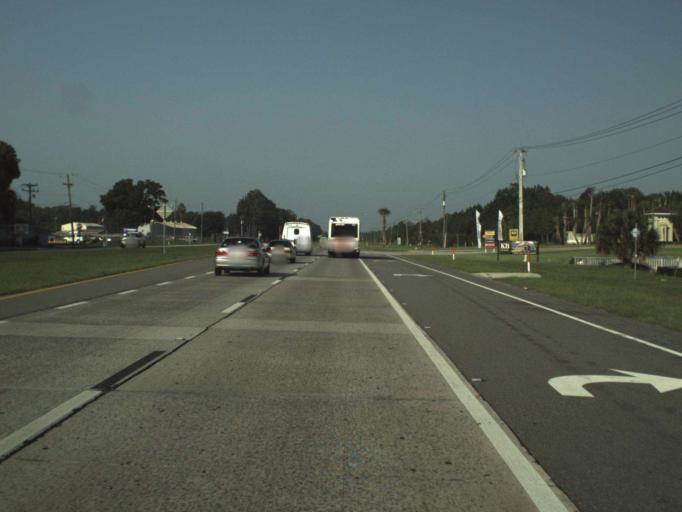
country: US
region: Florida
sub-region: Volusia County
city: Daytona Beach
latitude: 29.1624
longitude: -81.0933
